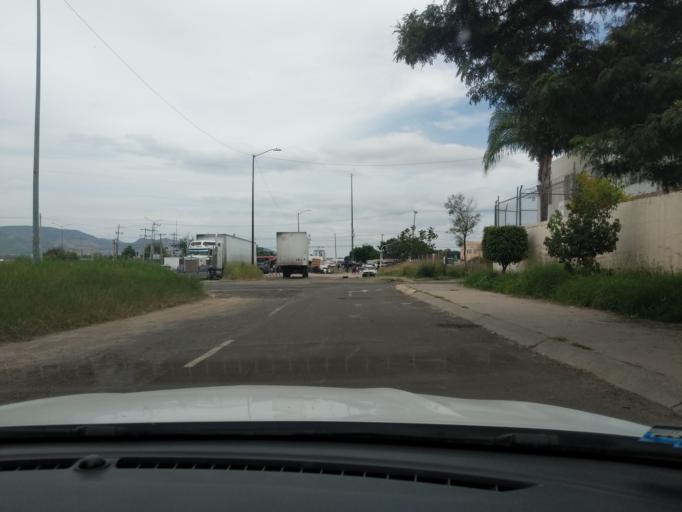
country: MX
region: Jalisco
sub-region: Zapopan
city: La Cuchilla (Extramuros de Tesistan)
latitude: 20.7803
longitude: -103.4631
